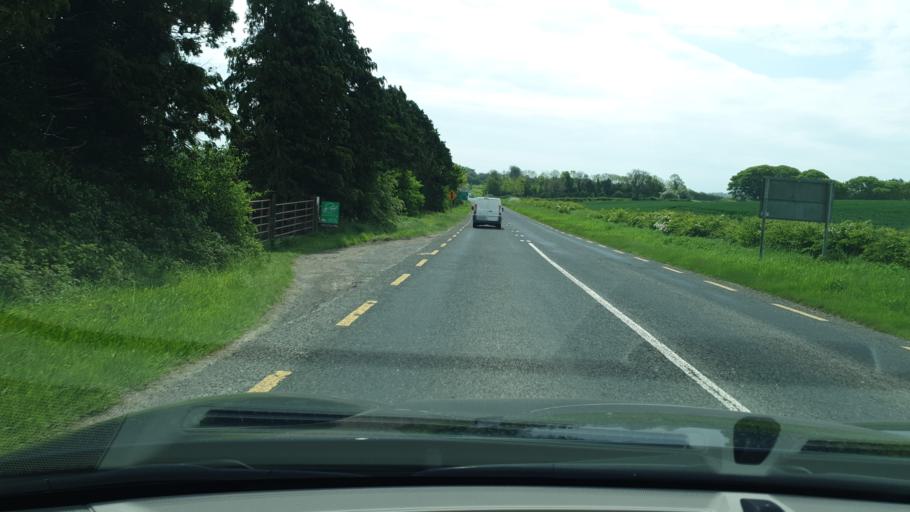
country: IE
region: Ulster
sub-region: An Cabhan
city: Kingscourt
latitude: 53.7897
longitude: -6.7357
